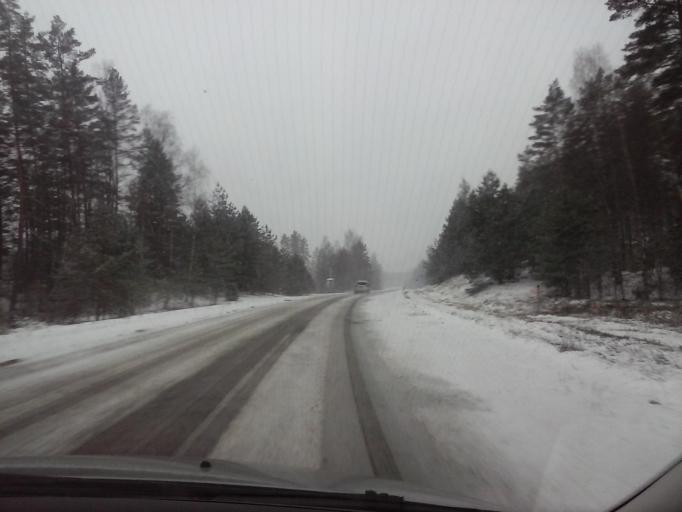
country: LV
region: Strenci
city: Seda
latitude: 57.6526
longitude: 25.8663
